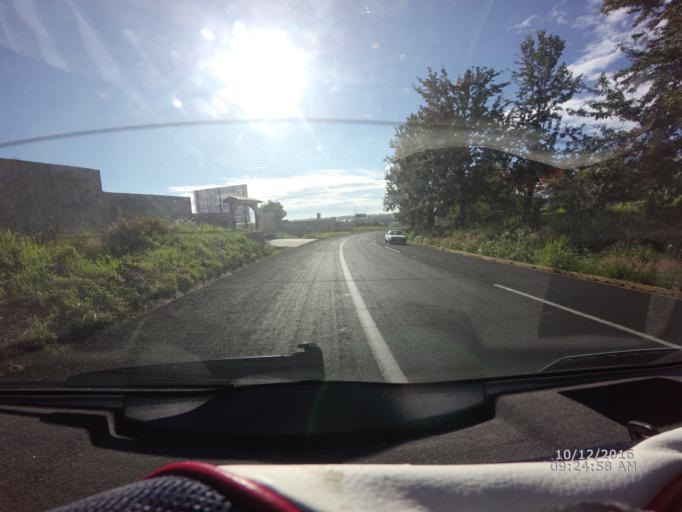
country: TR
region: Sivas
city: Sivas
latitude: 39.6811
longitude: 37.0540
